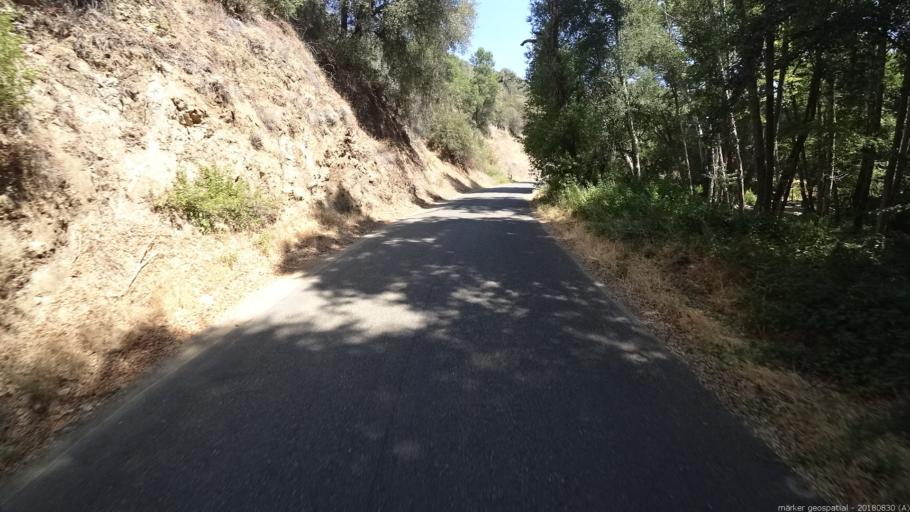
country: US
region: California
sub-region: Monterey County
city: King City
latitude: 36.0057
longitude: -121.3941
